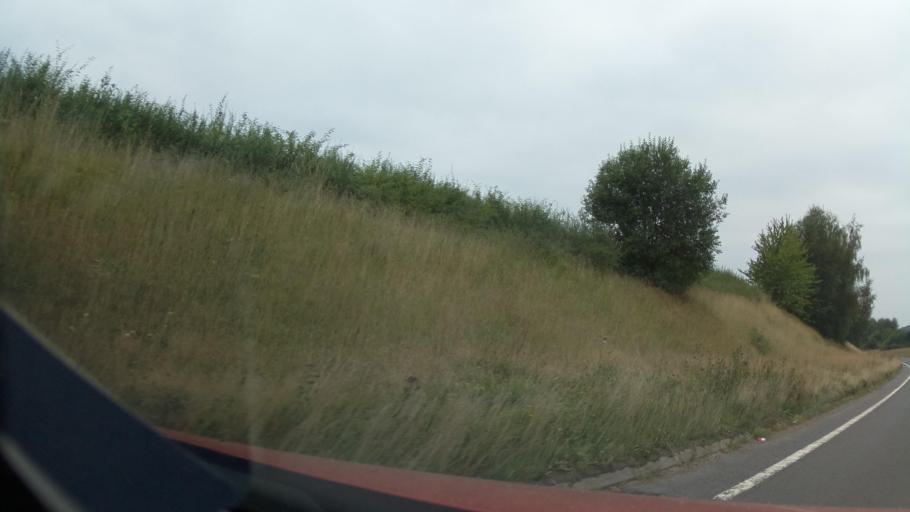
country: GB
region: England
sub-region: Shropshire
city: Stoke upon Tern
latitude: 52.8440
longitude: -2.5727
